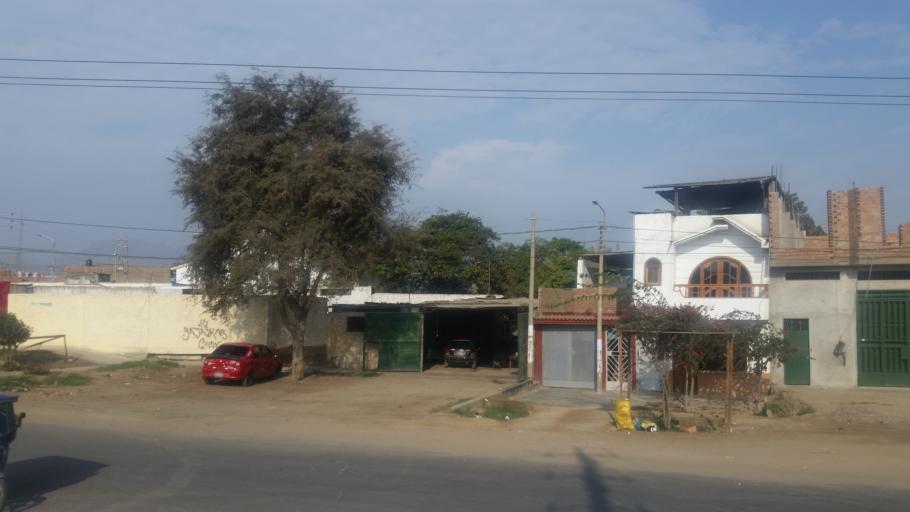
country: PE
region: La Libertad
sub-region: Chepen
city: Pacanga
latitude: -7.1585
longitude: -79.4418
